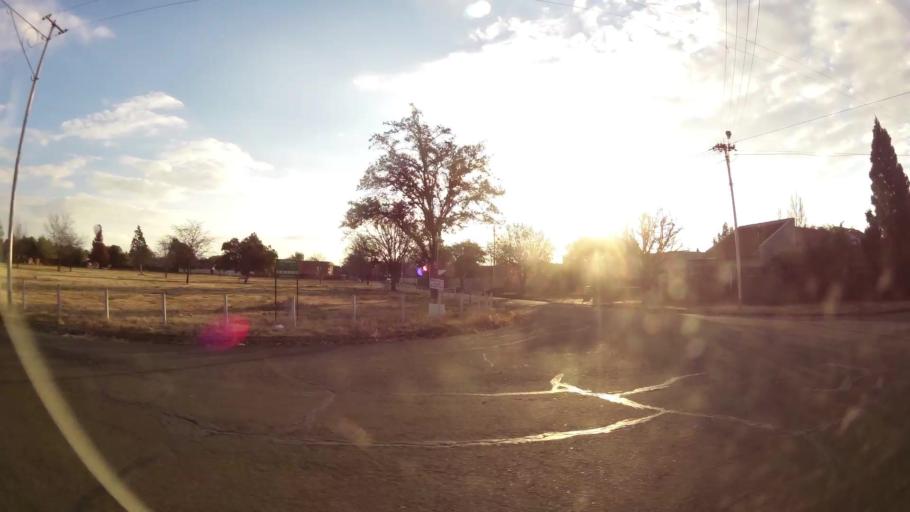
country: ZA
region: Orange Free State
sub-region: Mangaung Metropolitan Municipality
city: Bloemfontein
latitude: -29.1393
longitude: 26.1929
